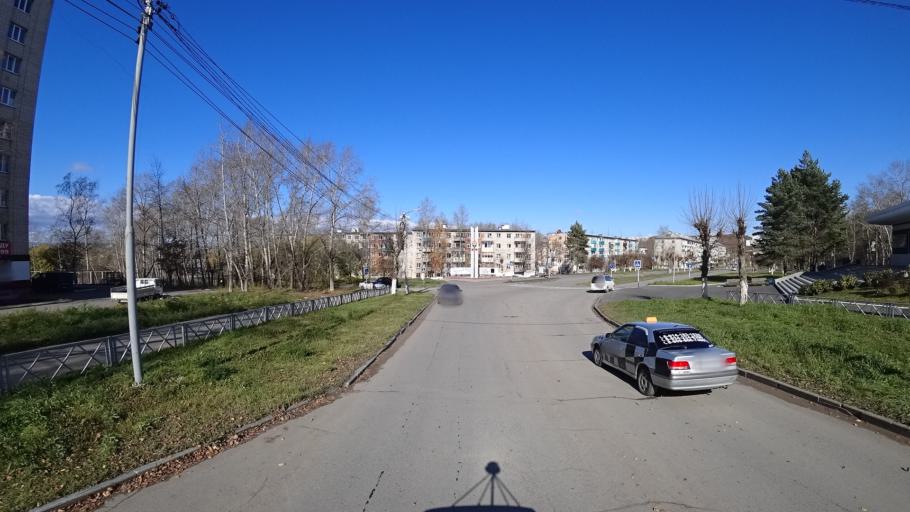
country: RU
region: Khabarovsk Krai
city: Amursk
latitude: 50.2219
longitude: 136.9032
